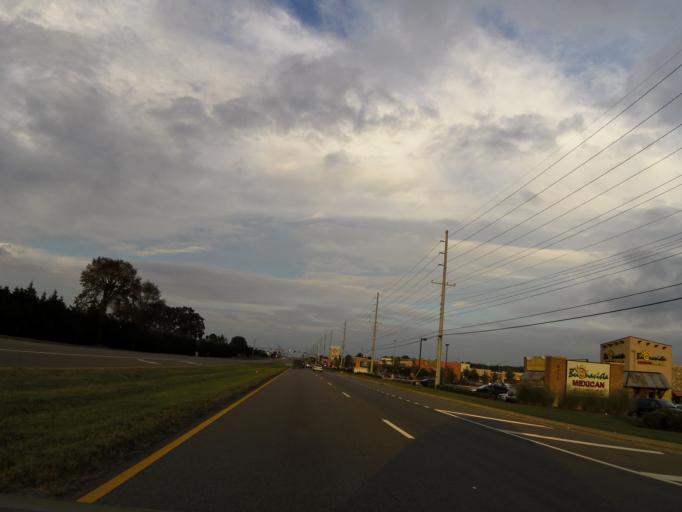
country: US
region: Alabama
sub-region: Madison County
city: Madison
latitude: 34.7505
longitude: -86.7583
